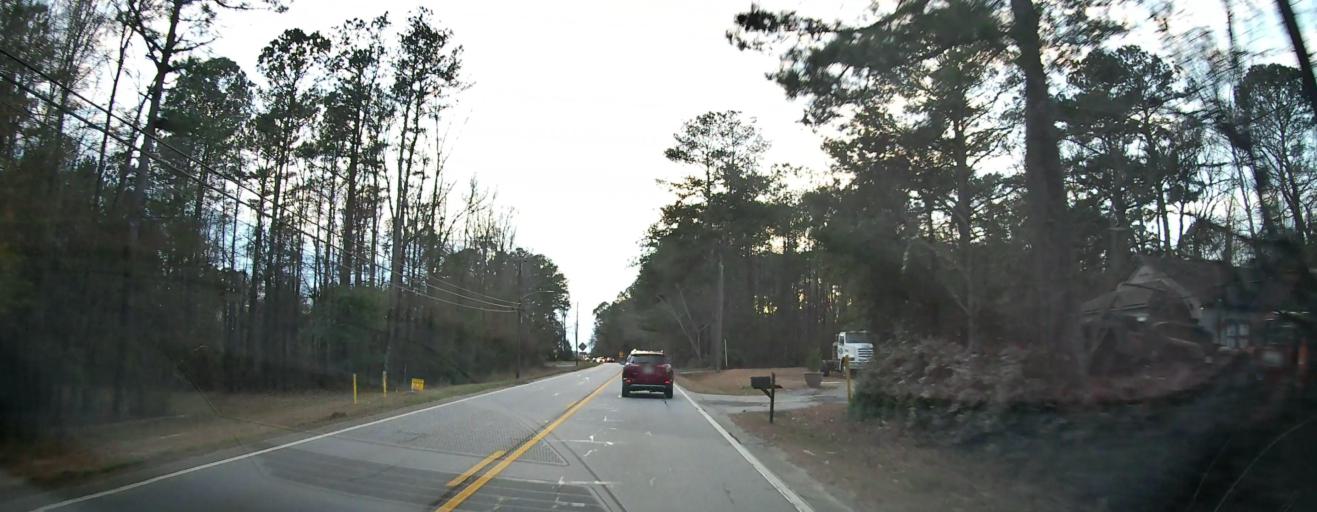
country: US
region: Alabama
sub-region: Russell County
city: Phenix City
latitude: 32.5752
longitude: -84.9175
